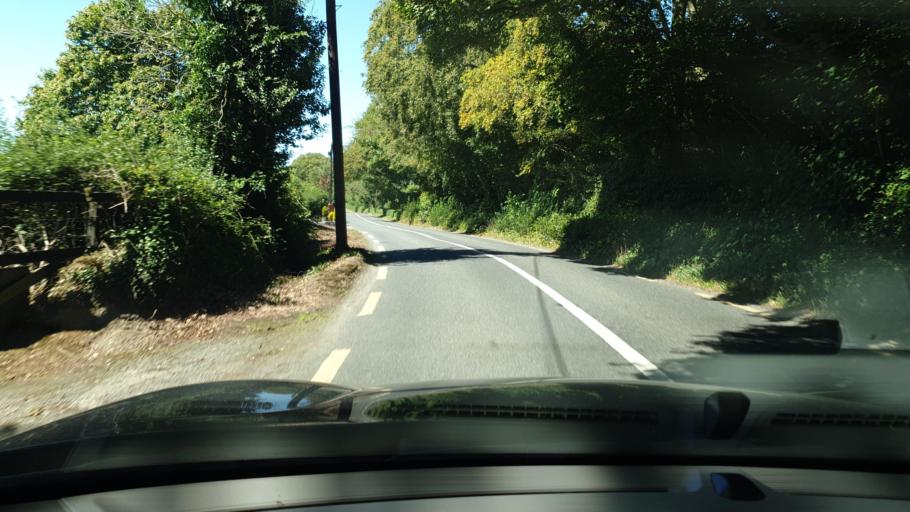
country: IE
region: Leinster
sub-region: An Mhi
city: Dunboyne
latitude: 53.4000
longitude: -6.4545
